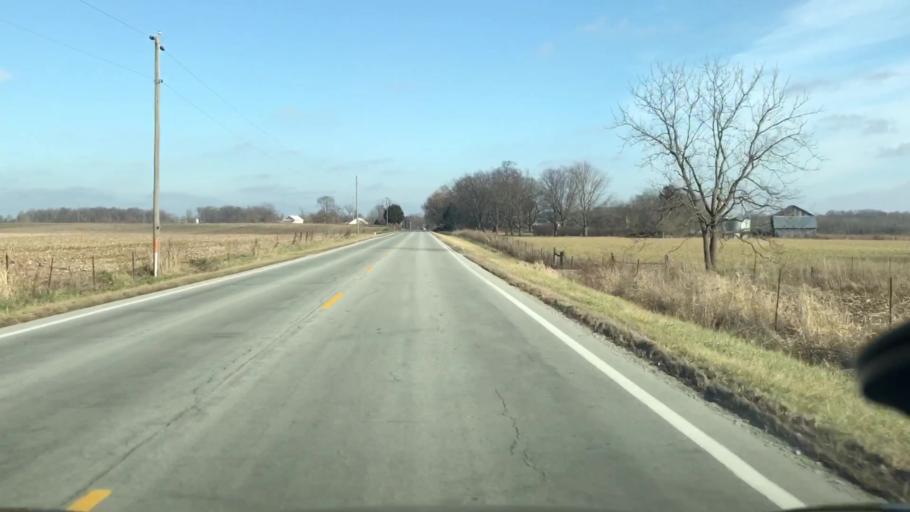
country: US
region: Ohio
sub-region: Greene County
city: Yellow Springs
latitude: 39.7962
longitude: -83.9333
